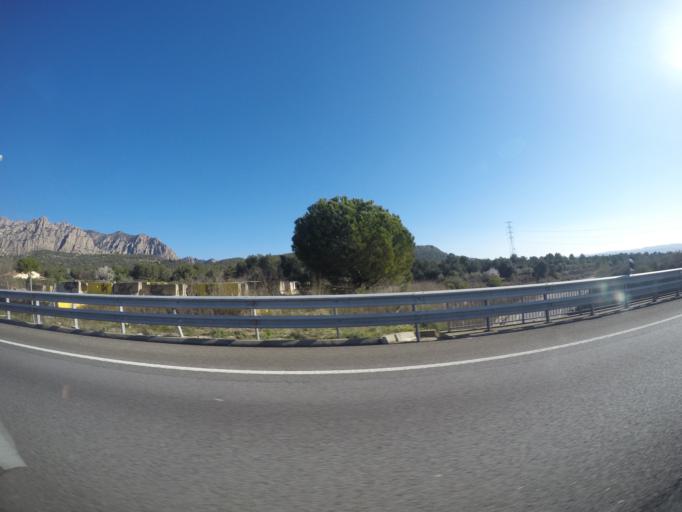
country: ES
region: Catalonia
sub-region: Provincia de Barcelona
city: Collbato
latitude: 41.5560
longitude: 1.8369
